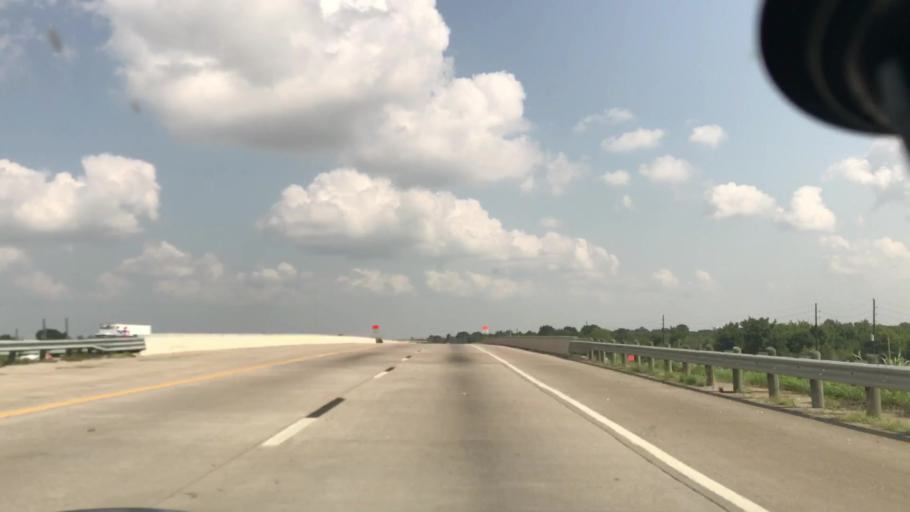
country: US
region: Texas
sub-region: Brazoria County
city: Iowa Colony
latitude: 29.5112
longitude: -95.3873
